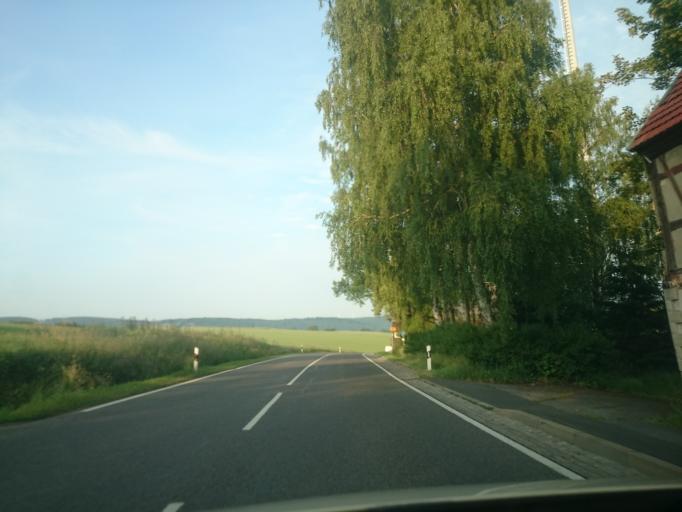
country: DE
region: Saxony
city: Pockau
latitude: 50.7121
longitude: 13.2499
